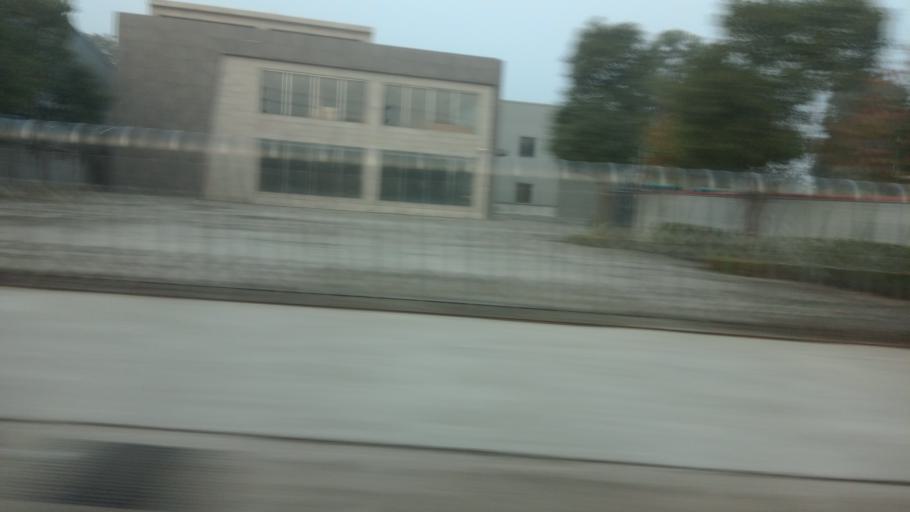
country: TW
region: Taiwan
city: Daxi
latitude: 24.9057
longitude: 121.2306
